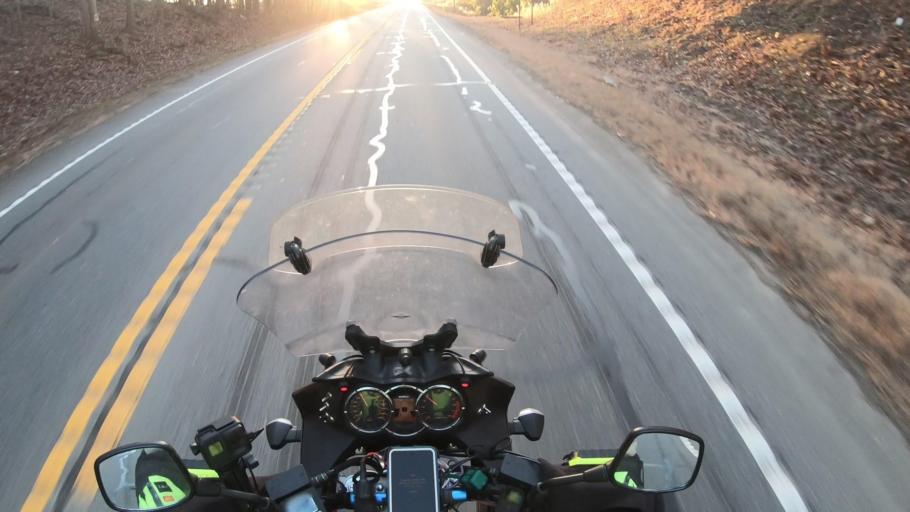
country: US
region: Georgia
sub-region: Forsyth County
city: Cumming
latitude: 34.3014
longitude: -84.2222
